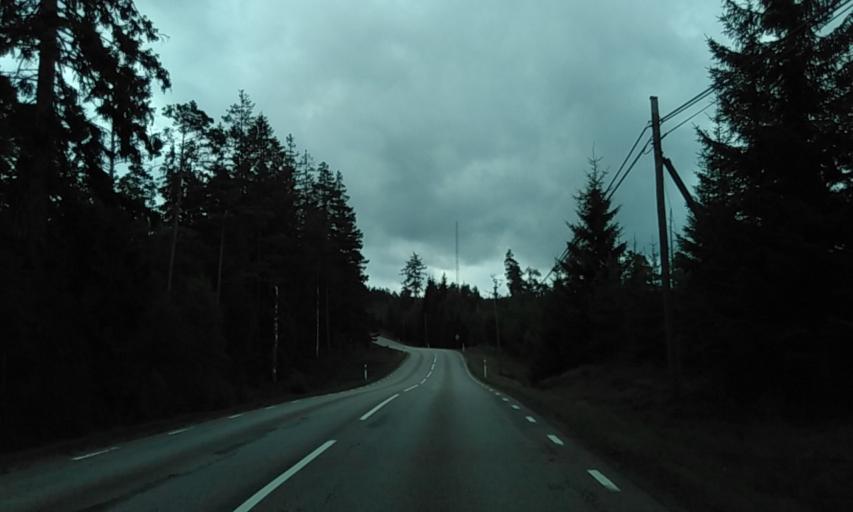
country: SE
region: Vaestra Goetaland
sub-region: Alingsas Kommun
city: Alingsas
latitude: 57.8493
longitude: 12.6363
